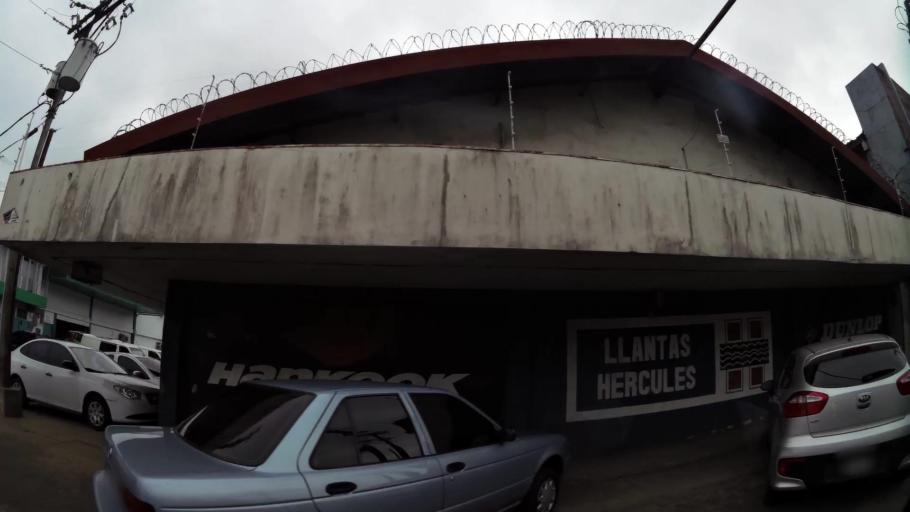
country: PA
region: Panama
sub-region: Distrito de Panama
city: Ancon
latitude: 8.9727
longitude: -79.5402
